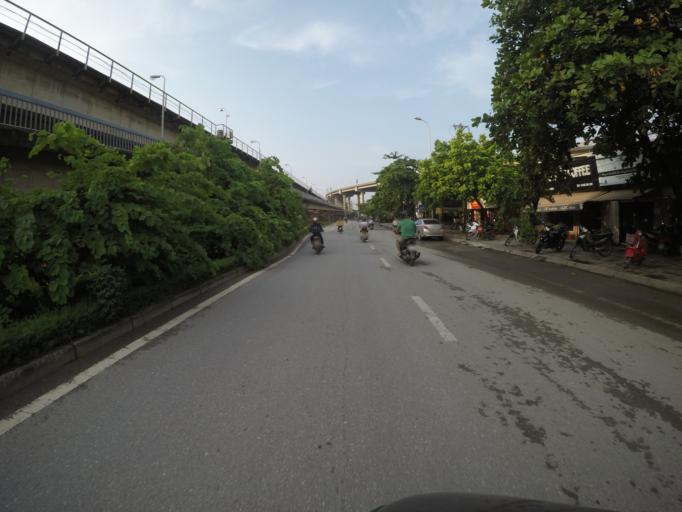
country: VN
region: Ha Noi
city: Tay Ho
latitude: 21.0873
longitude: 105.7858
